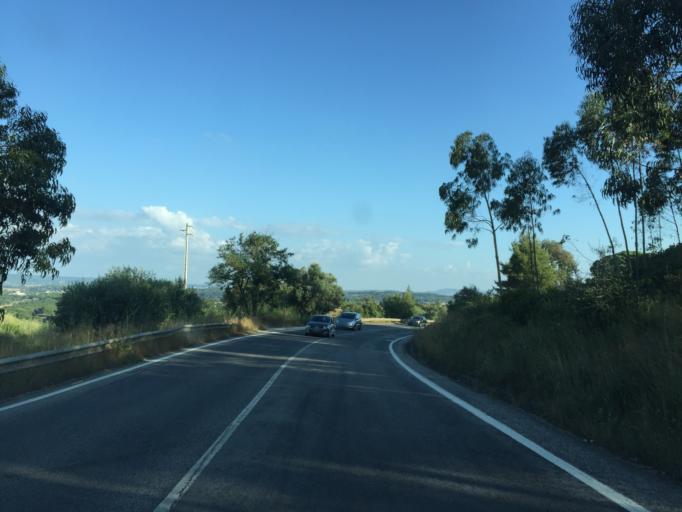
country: PT
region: Lisbon
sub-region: Alenquer
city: Alenquer
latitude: 39.1255
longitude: -8.9914
